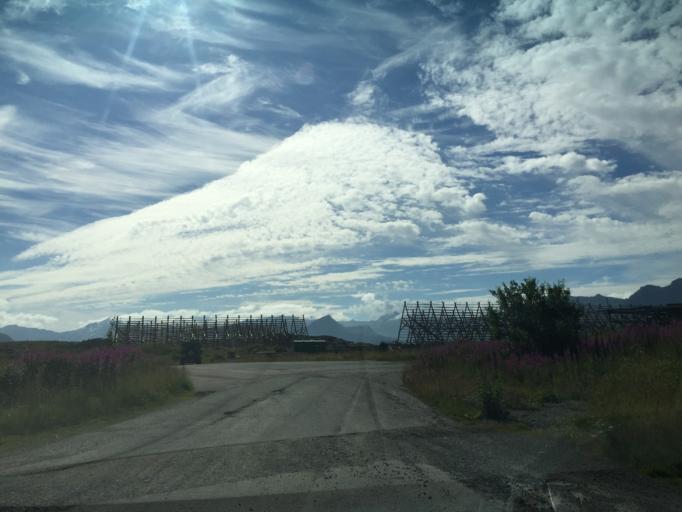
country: NO
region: Nordland
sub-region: Vagan
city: Kabelvag
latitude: 68.3862
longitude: 14.4093
